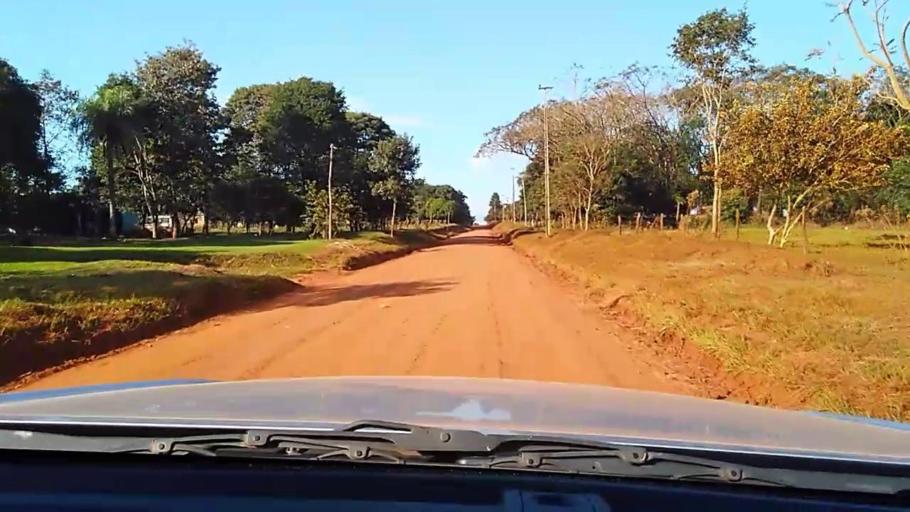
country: PY
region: Alto Parana
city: Doctor Juan Leon Mallorquin
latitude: -25.6880
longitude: -55.3771
